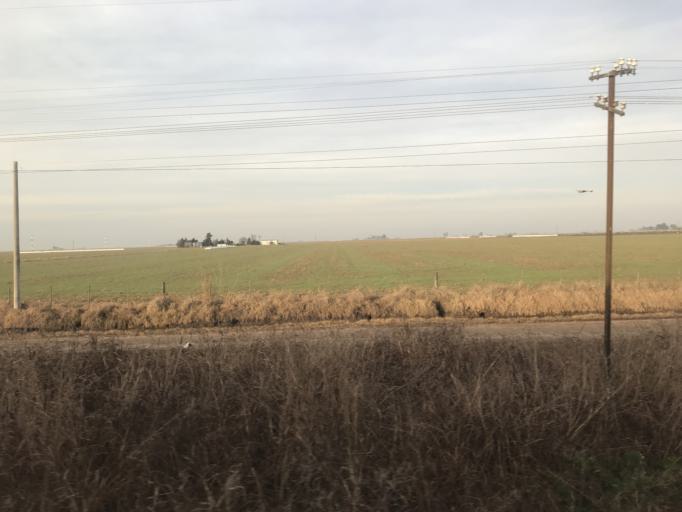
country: AR
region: Cordoba
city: Marcos Juarez
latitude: -32.6839
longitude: -62.1921
